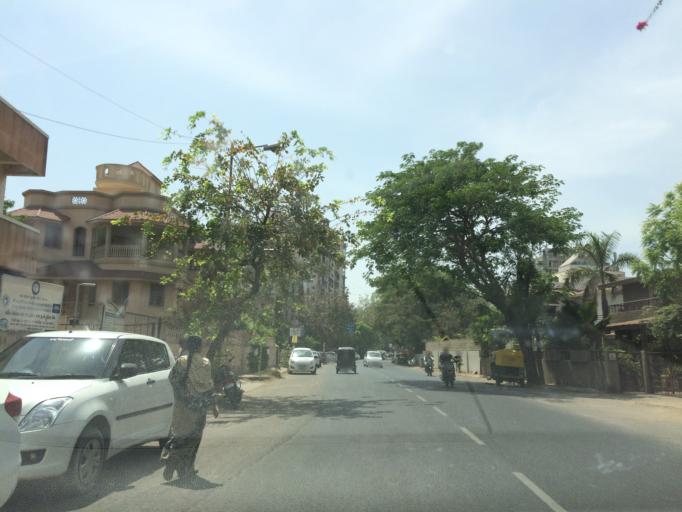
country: IN
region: Gujarat
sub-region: Ahmadabad
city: Ahmedabad
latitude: 23.0094
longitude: 72.5506
